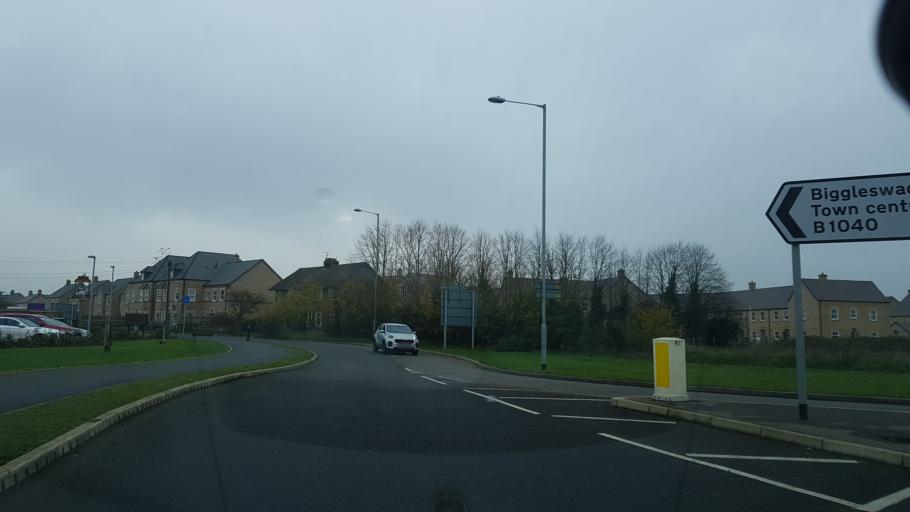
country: GB
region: England
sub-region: Central Bedfordshire
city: Biggleswade
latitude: 52.0999
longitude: -0.2474
